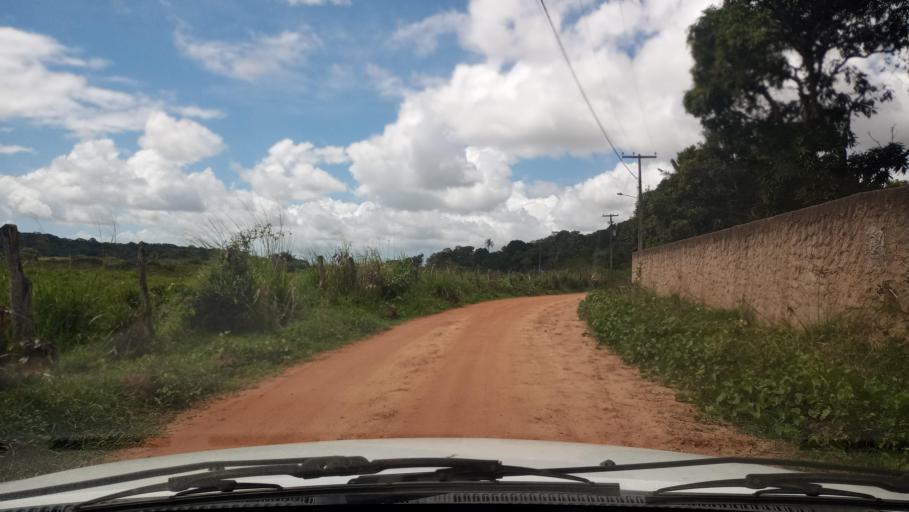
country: BR
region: Rio Grande do Norte
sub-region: Goianinha
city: Goianinha
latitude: -6.2611
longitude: -35.2546
